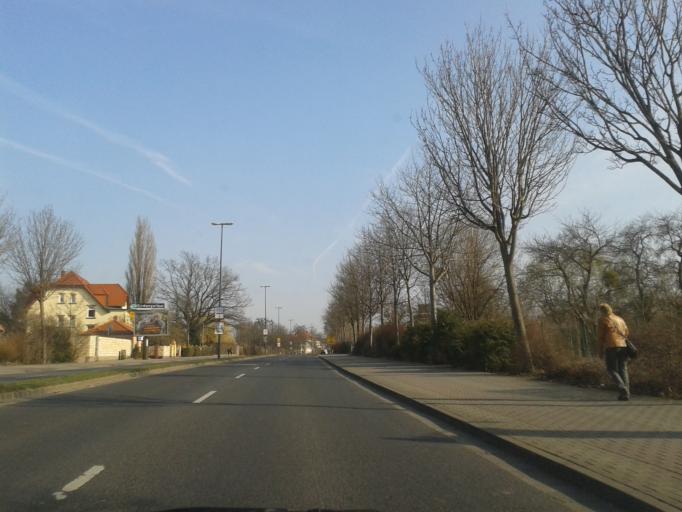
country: DE
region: Saxony
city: Dresden
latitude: 51.0118
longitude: 13.7803
